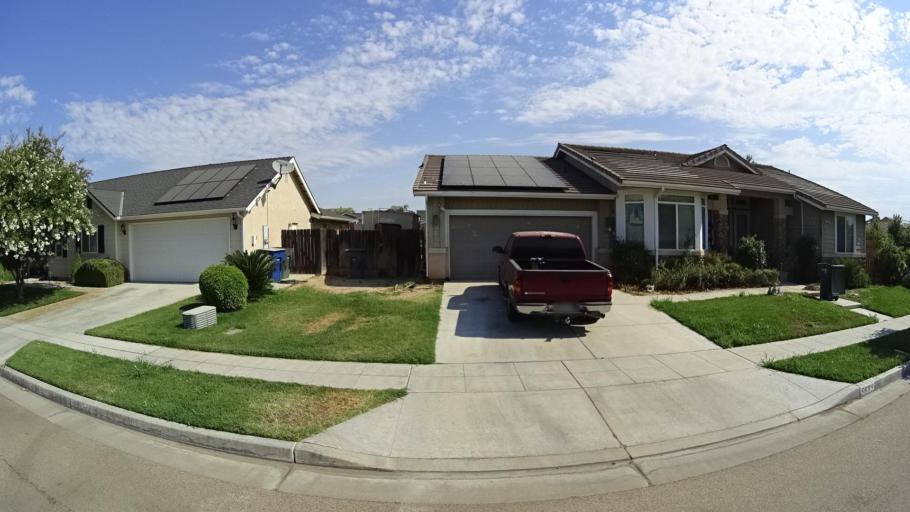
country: US
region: California
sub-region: Fresno County
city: Sunnyside
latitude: 36.7087
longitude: -119.6874
